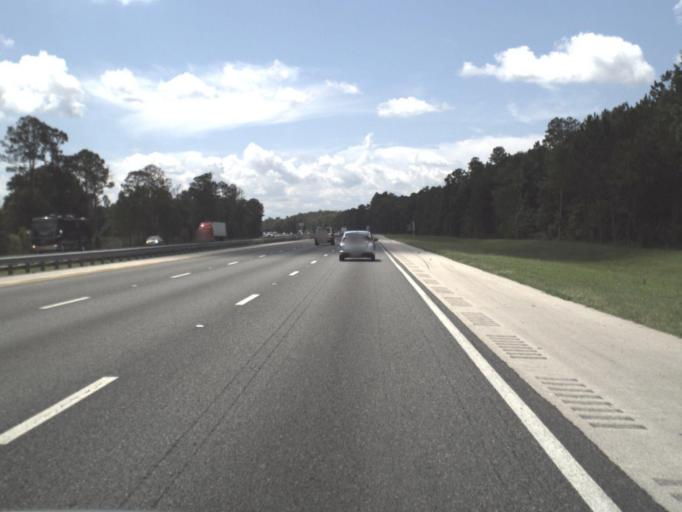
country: US
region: Florida
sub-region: Saint Johns County
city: Villano Beach
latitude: 29.9590
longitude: -81.4456
